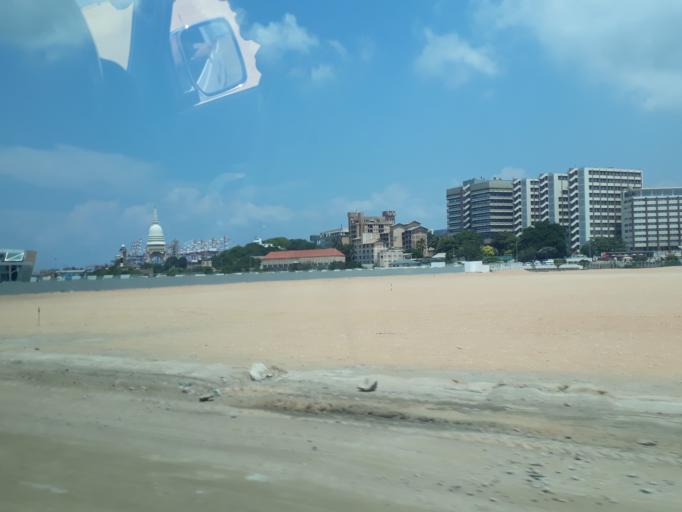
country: LK
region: Western
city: Colombo
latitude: 6.9317
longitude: 79.8390
